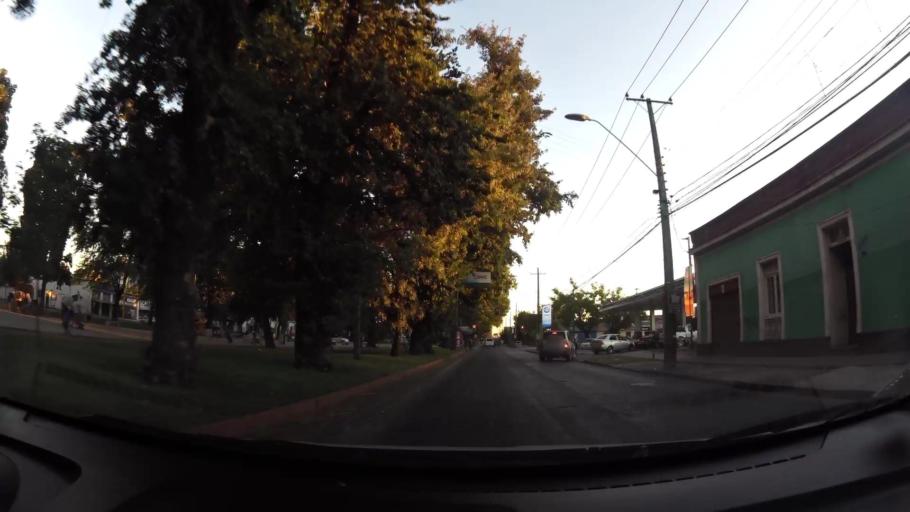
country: CL
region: Maule
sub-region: Provincia de Curico
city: Curico
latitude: -34.9884
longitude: -71.2340
